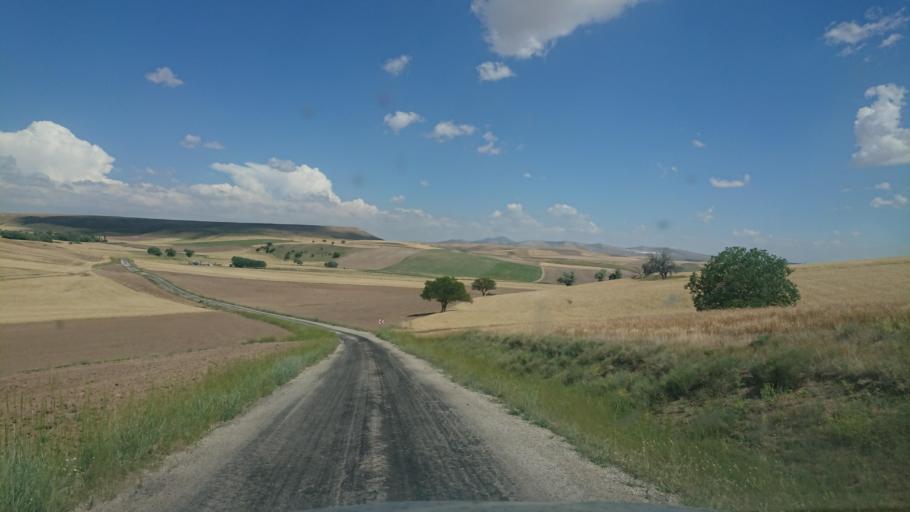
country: TR
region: Aksaray
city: Agacoren
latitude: 38.8006
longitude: 33.8170
